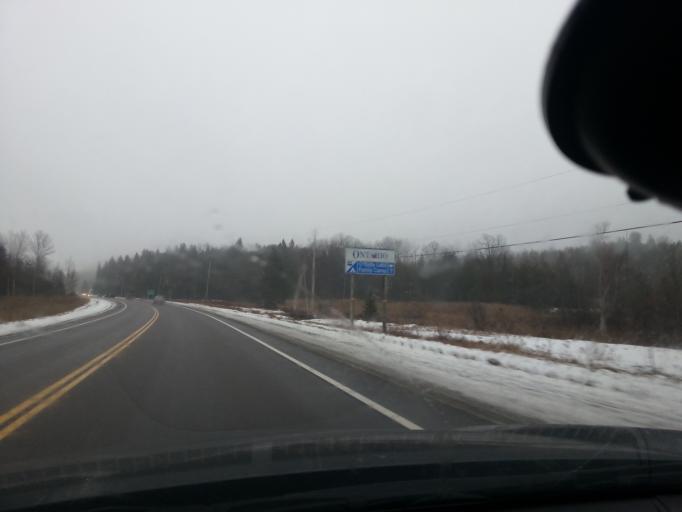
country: CA
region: Ontario
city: Skatepark
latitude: 44.7515
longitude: -76.8310
